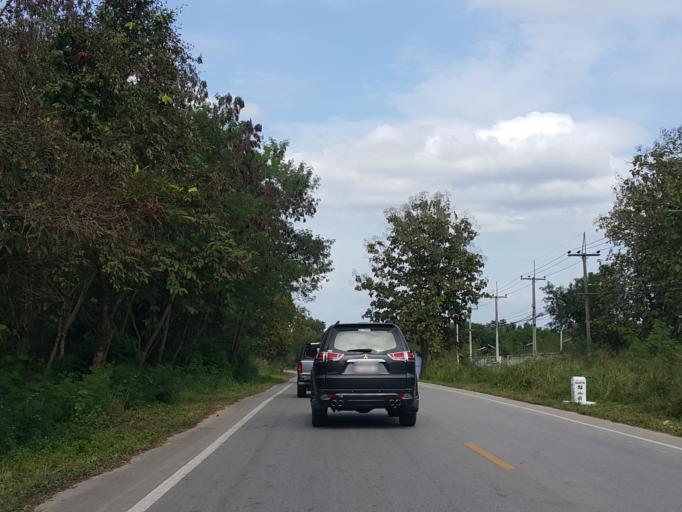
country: TH
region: Lampang
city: Lampang
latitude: 18.3612
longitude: 99.4588
